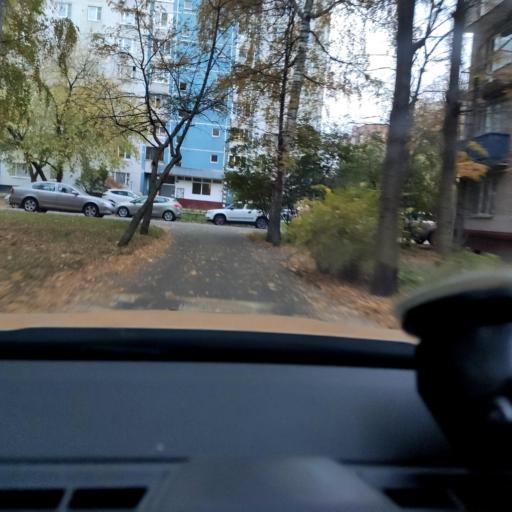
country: RU
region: Moscow
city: Vatutino
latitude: 55.8674
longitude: 37.6727
